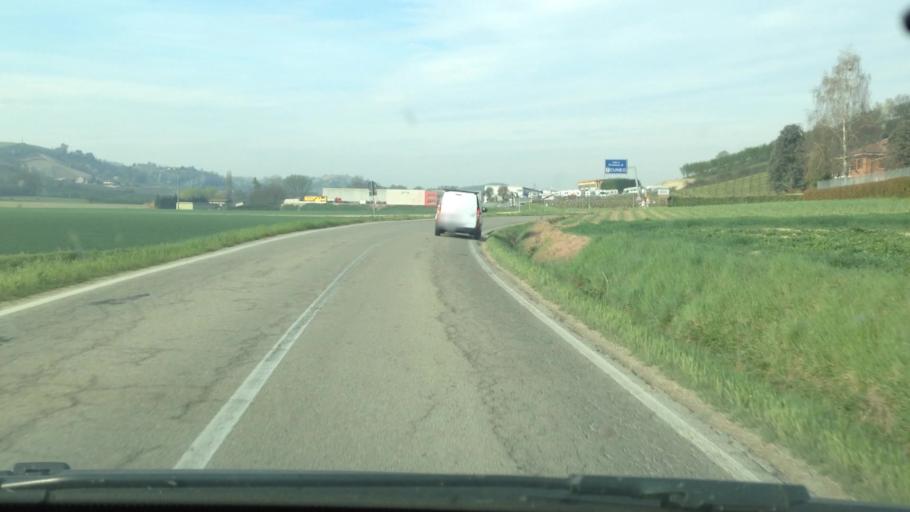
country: IT
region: Piedmont
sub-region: Provincia di Cuneo
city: Castellinaldo
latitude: 44.8091
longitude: 8.0362
